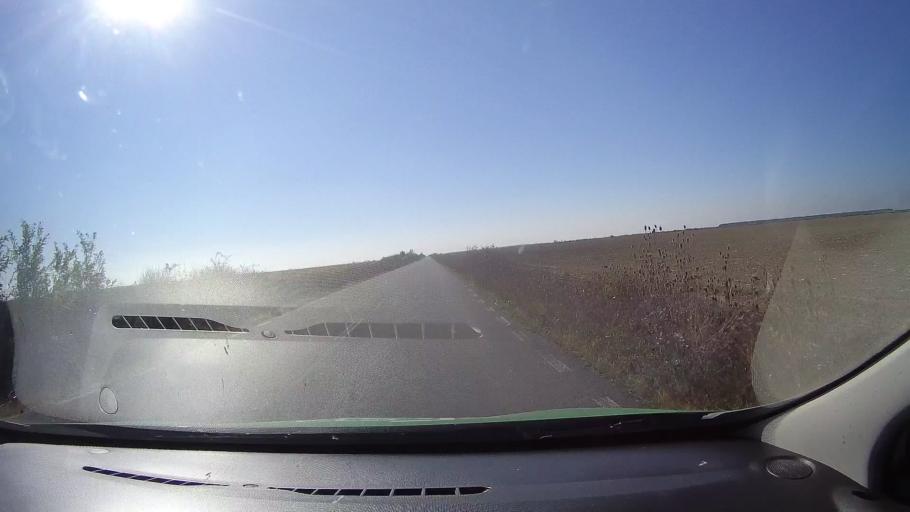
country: RO
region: Satu Mare
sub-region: Municipiul Satu Mare
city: Satmarel
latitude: 47.6974
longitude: 22.7670
